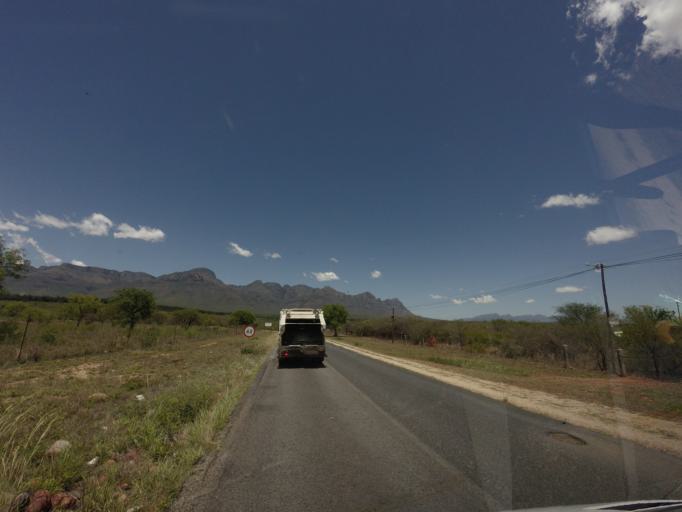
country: ZA
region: Limpopo
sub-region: Mopani District Municipality
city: Hoedspruit
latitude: -24.4009
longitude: 30.8040
